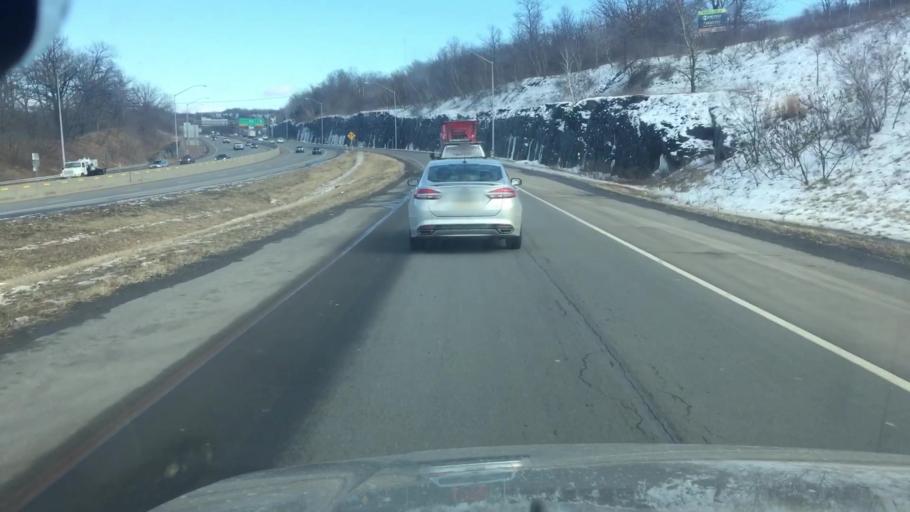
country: US
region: Pennsylvania
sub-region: Luzerne County
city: Hudson
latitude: 41.2506
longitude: -75.8342
